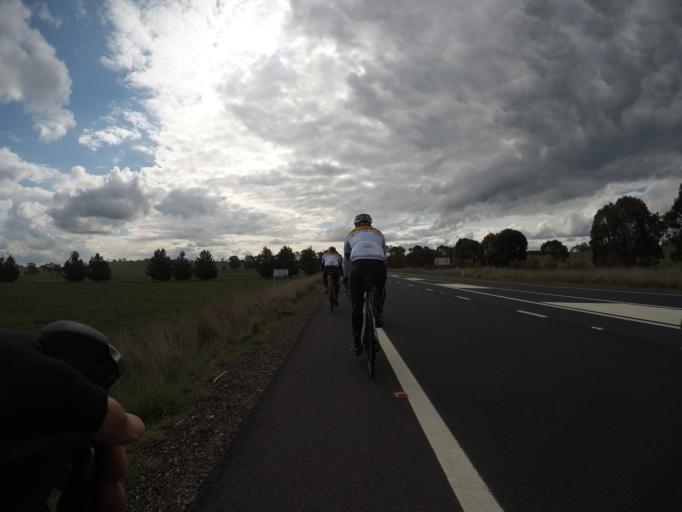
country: AU
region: New South Wales
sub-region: Blayney
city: Millthorpe
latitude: -33.3899
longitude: 149.2215
